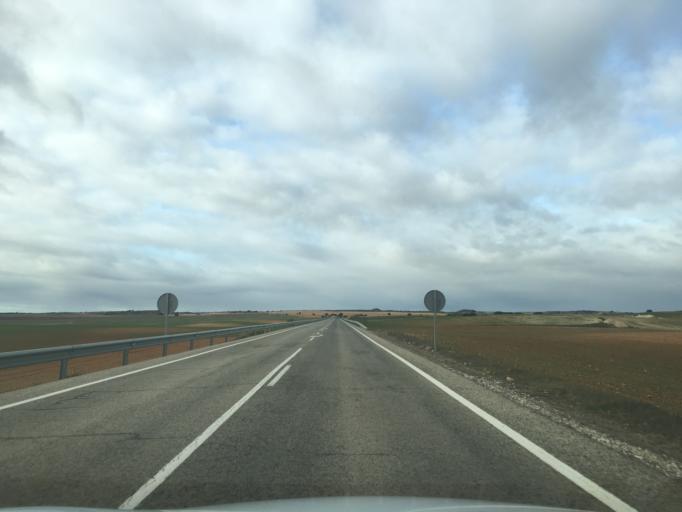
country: ES
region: Castille-La Mancha
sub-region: Provincia de Albacete
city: Petrola
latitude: 38.8262
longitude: -1.5753
